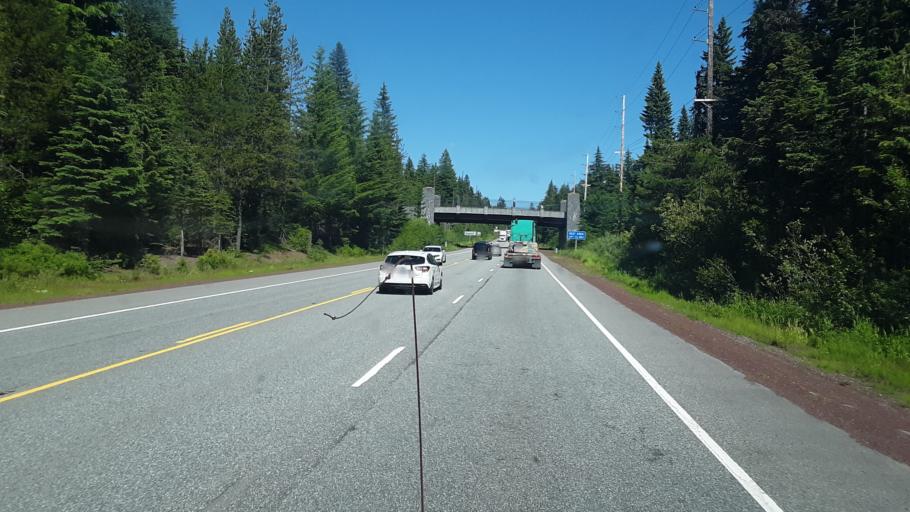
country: US
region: Oregon
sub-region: Clackamas County
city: Mount Hood Village
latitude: 45.3024
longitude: -121.7582
